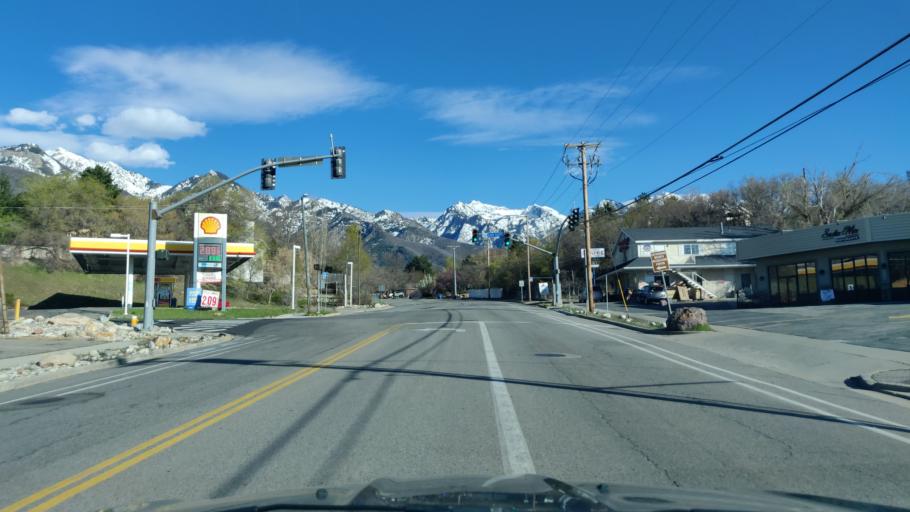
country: US
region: Utah
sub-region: Salt Lake County
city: Cottonwood Heights
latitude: 40.6107
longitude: -111.8185
